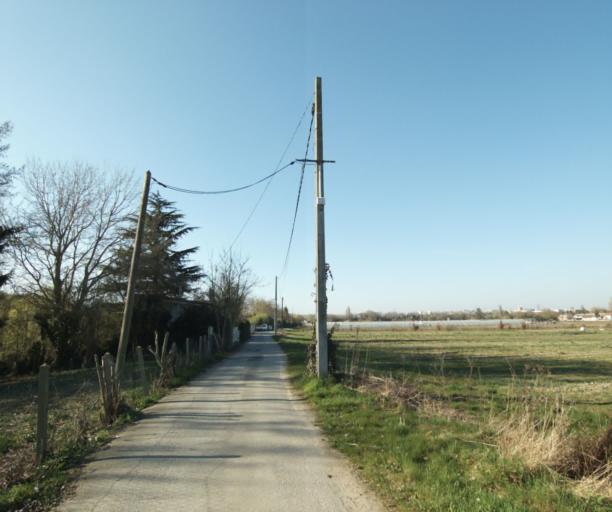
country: FR
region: Ile-de-France
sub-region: Departement du Val-d'Oise
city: Neuville-sur-Oise
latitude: 49.0226
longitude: 2.0688
